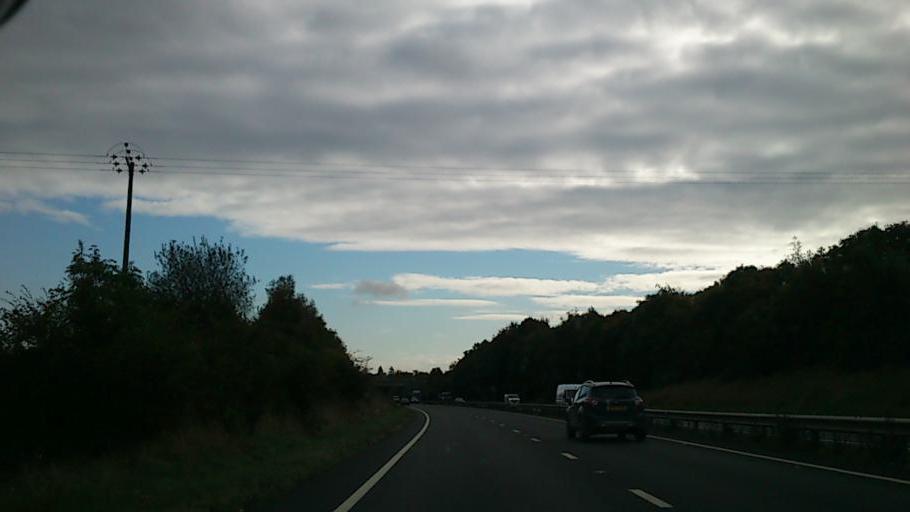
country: GB
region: England
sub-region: Shropshire
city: Great Hanwood
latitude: 52.6842
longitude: -2.7894
